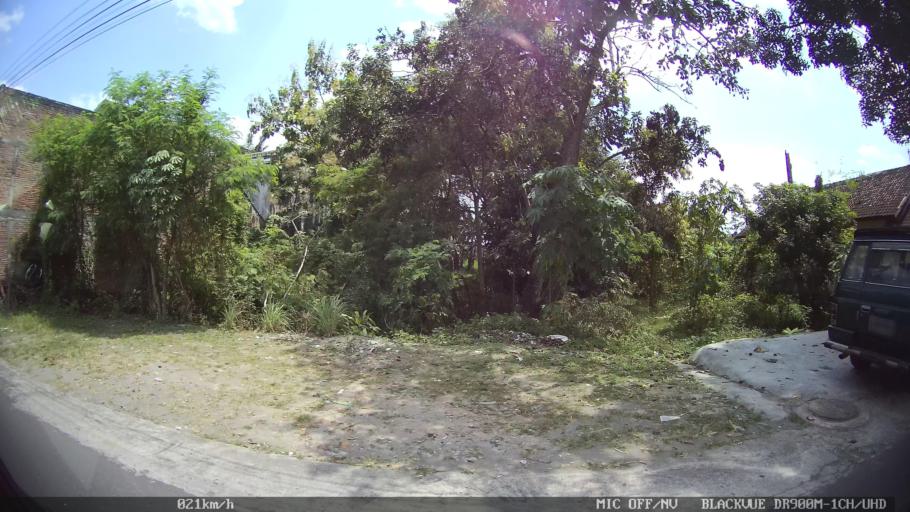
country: ID
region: Daerah Istimewa Yogyakarta
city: Kasihan
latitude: -7.8117
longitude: 110.3433
